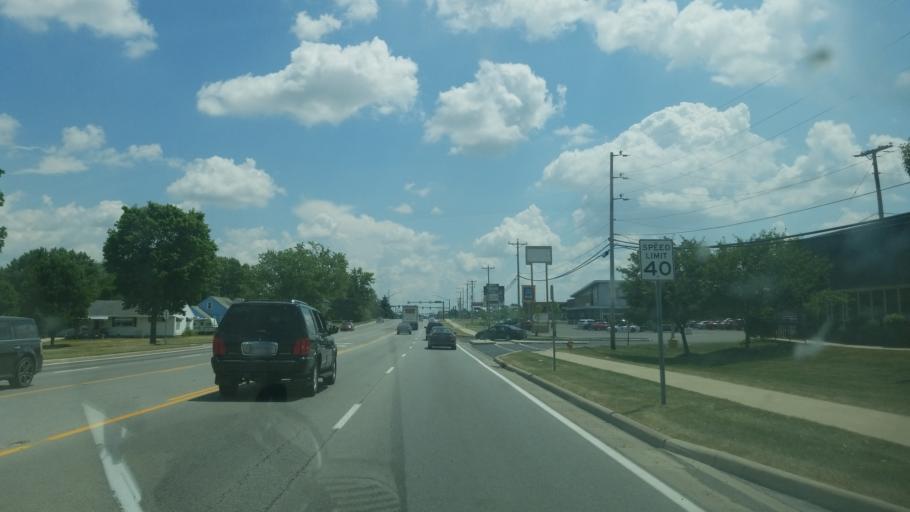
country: US
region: Ohio
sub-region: Allen County
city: Lima
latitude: 40.7306
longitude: -84.0657
